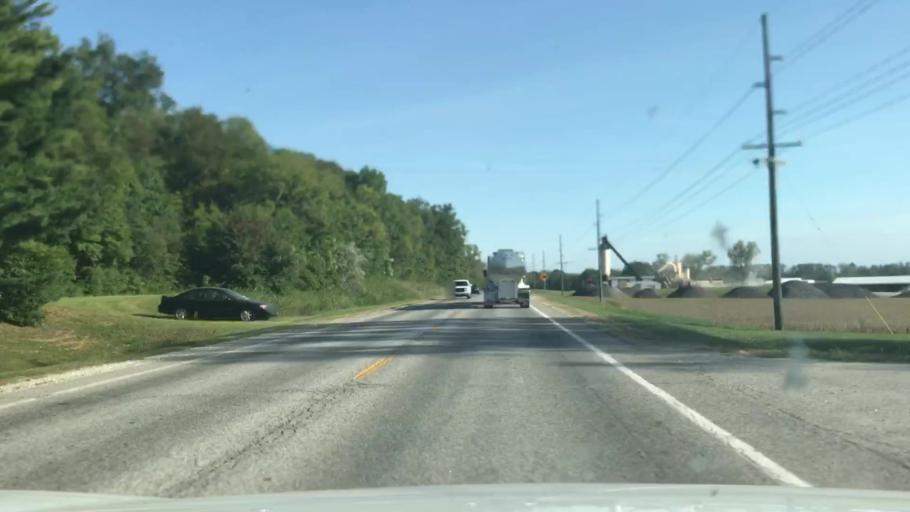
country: US
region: Illinois
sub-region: Adams County
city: Quincy
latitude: 39.8519
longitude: -91.3809
